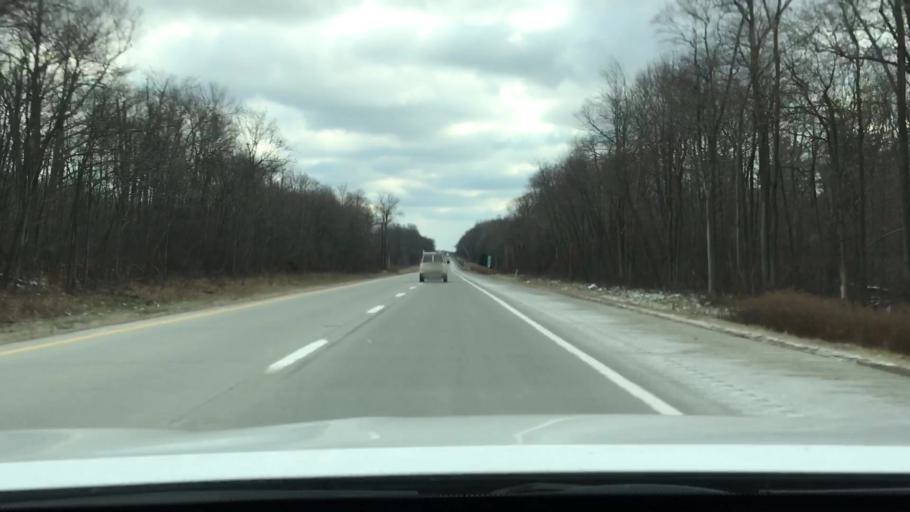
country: US
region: Pennsylvania
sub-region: Monroe County
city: Mount Pocono
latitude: 41.1546
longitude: -75.4131
